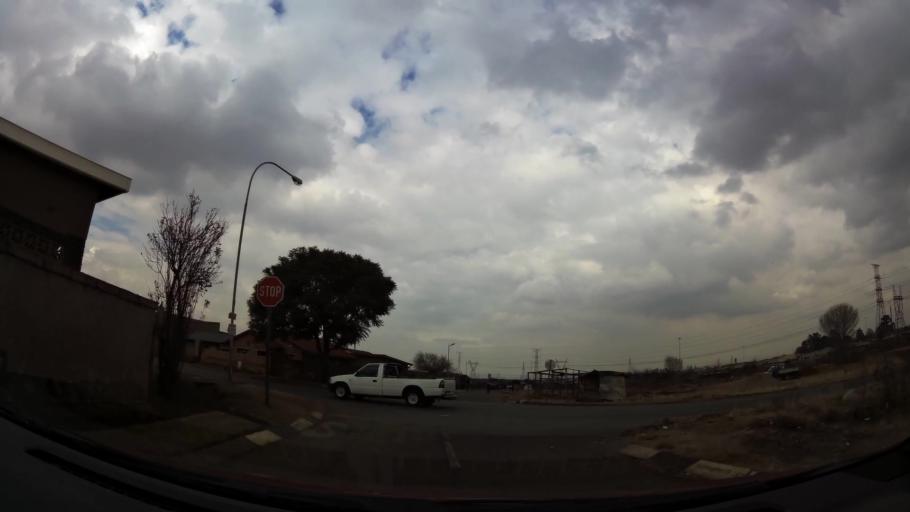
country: ZA
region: Gauteng
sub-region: City of Johannesburg Metropolitan Municipality
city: Soweto
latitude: -26.2592
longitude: 27.8389
